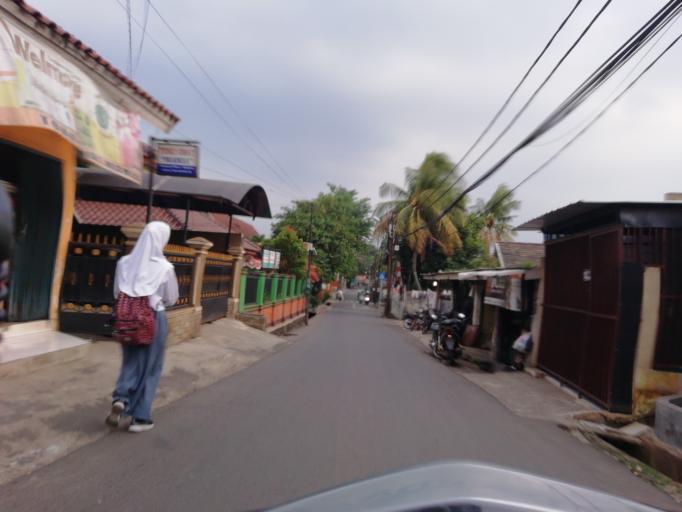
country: ID
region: West Java
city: Depok
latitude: -6.3272
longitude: 106.8203
